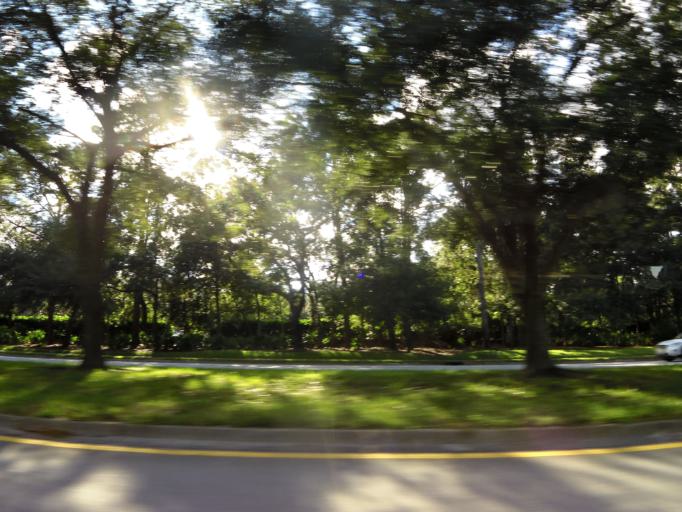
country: US
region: Florida
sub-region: Duval County
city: Jacksonville Beach
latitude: 30.2645
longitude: -81.4374
